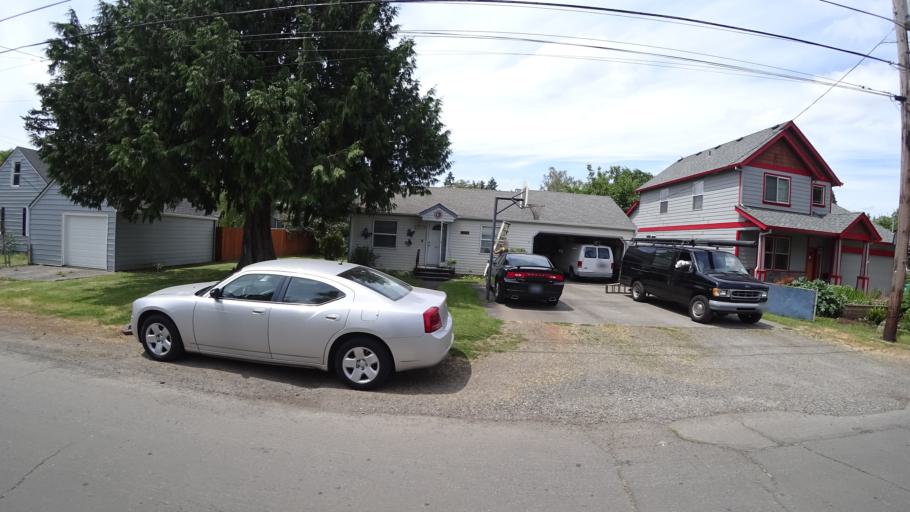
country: US
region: Oregon
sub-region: Multnomah County
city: Lents
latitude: 45.4690
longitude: -122.5933
